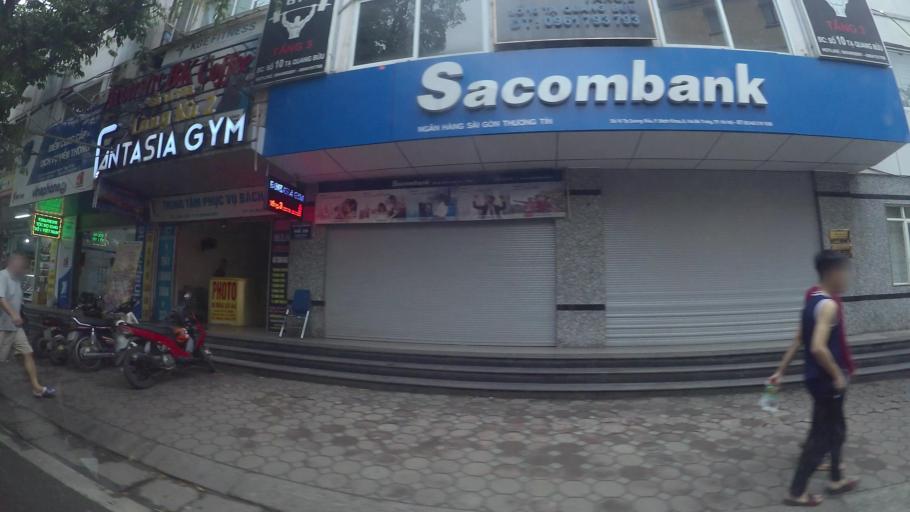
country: VN
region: Ha Noi
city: Hai BaTrung
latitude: 21.0053
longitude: 105.8470
